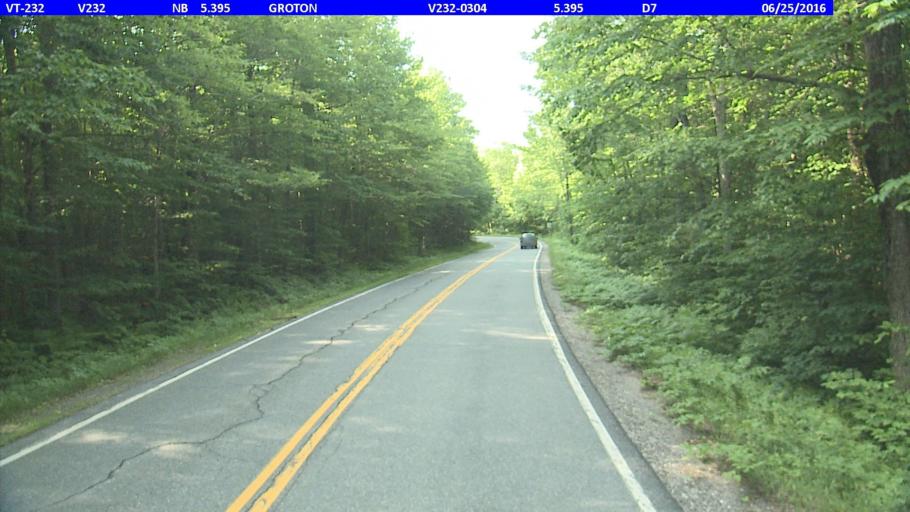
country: US
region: Vermont
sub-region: Washington County
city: Barre
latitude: 44.2772
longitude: -72.2851
